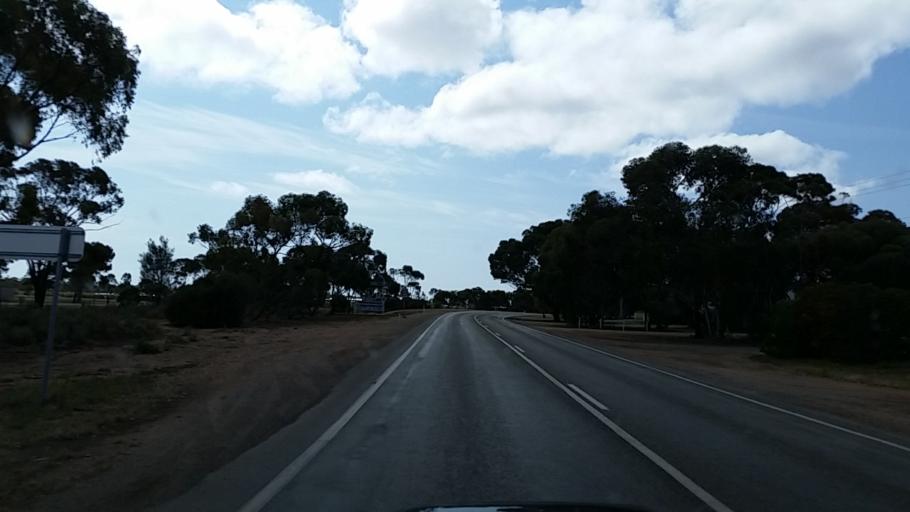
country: AU
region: South Australia
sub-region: Port Pirie City and Dists
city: Port Pirie
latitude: -33.2149
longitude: 138.0107
